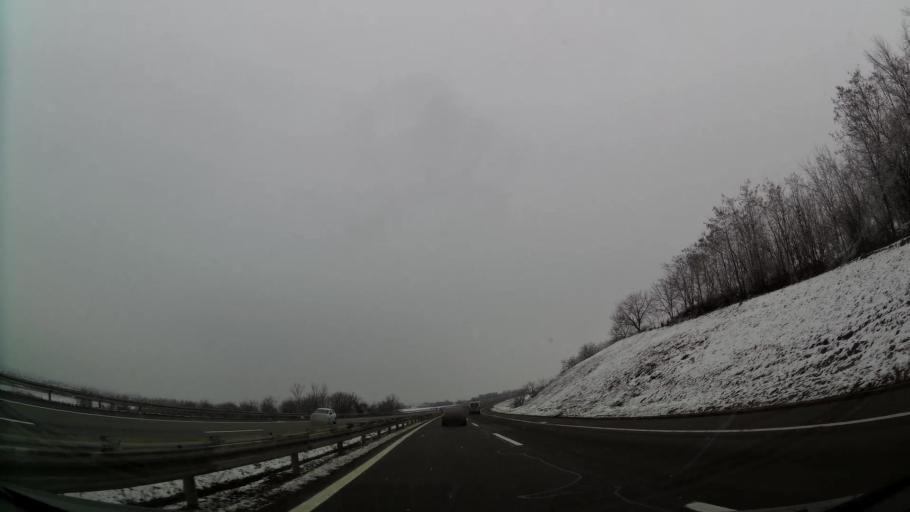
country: RS
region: Central Serbia
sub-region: Pomoravski Okrug
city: Paracin
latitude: 43.8354
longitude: 21.4273
